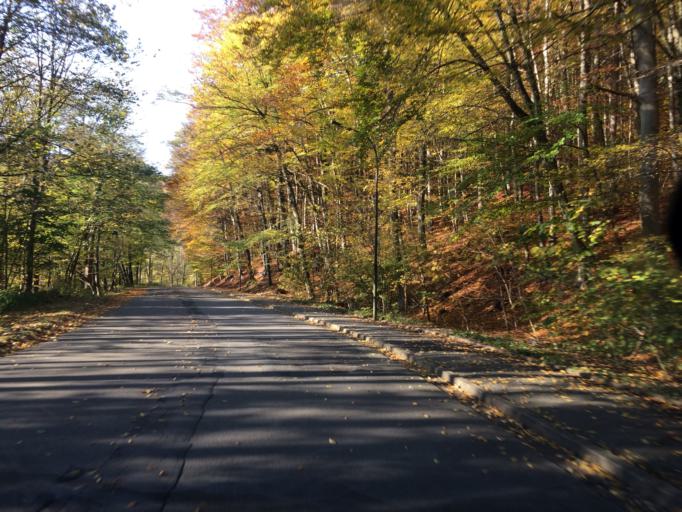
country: DE
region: Lower Saxony
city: Bad Lauterberg im Harz
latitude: 51.6387
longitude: 10.4867
